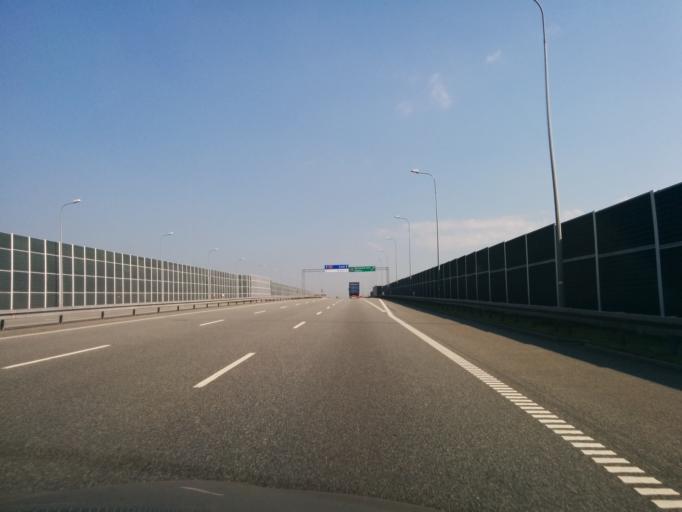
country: PL
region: Silesian Voivodeship
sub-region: Powiat tarnogorski
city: Wieszowa
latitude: 50.3417
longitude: 18.7266
